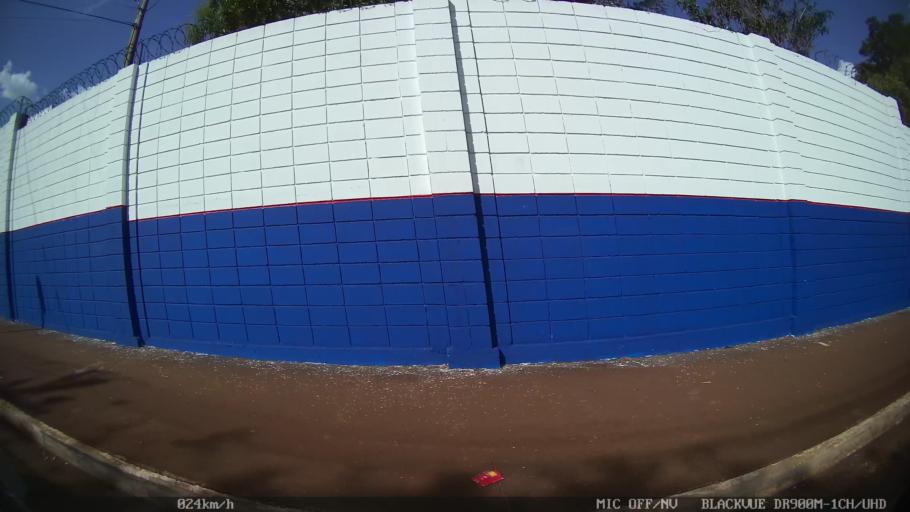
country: BR
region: Sao Paulo
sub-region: Ribeirao Preto
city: Ribeirao Preto
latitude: -21.2049
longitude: -47.8592
